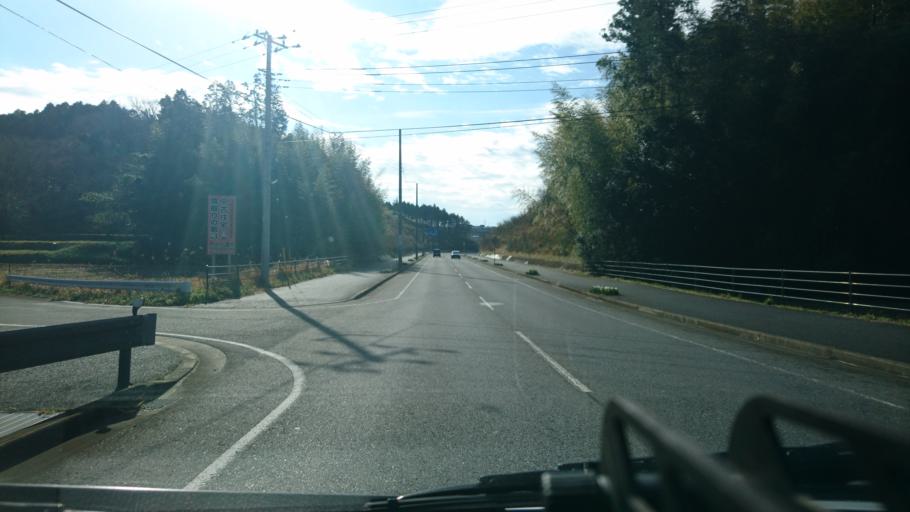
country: JP
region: Chiba
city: Kisarazu
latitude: 35.3529
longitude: 139.9423
